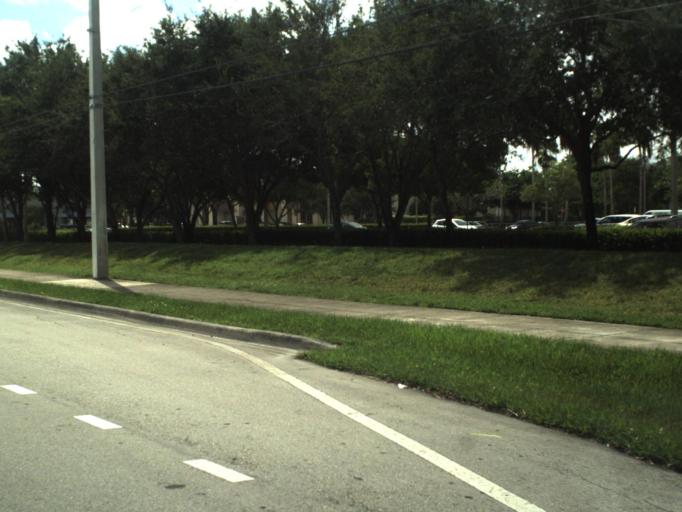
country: US
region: Florida
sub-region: Broward County
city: Sunshine Ranches
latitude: 26.0076
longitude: -80.3012
